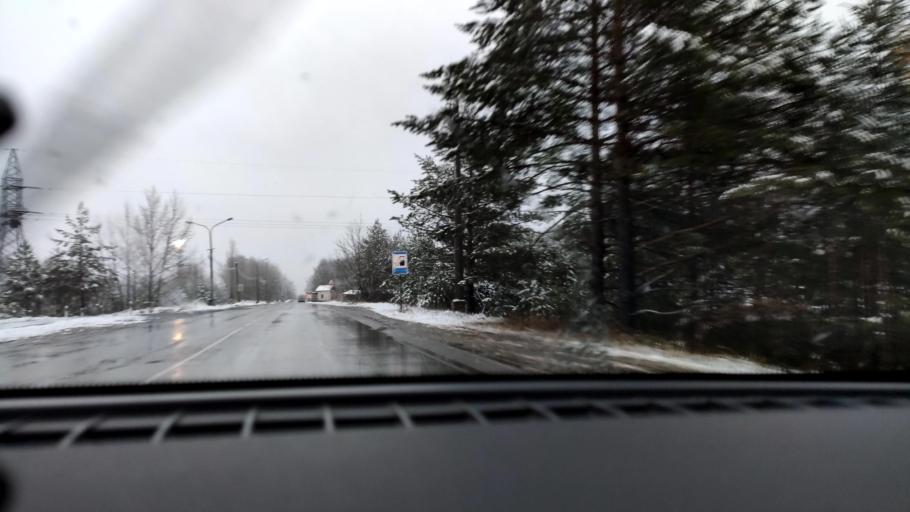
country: RU
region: Perm
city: Overyata
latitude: 58.0158
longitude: 55.8941
